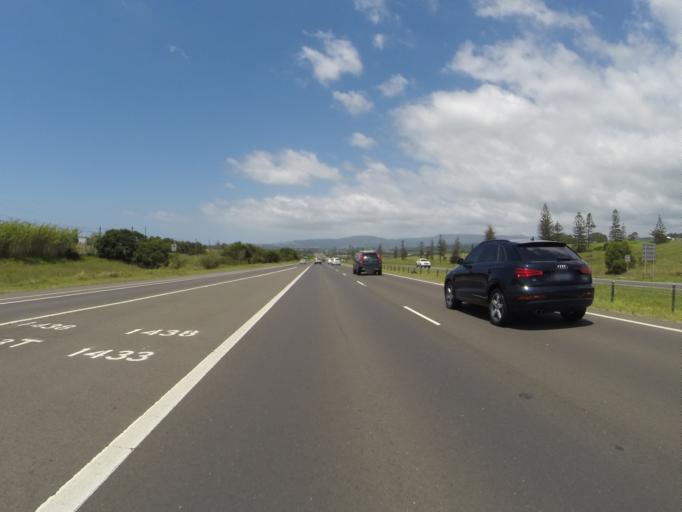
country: AU
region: New South Wales
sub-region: Shellharbour
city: Croom
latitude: -34.5922
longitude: 150.8438
